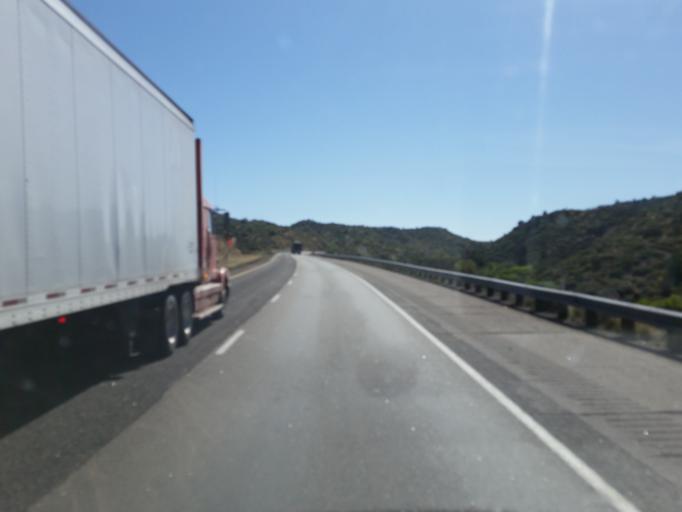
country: US
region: Arizona
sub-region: Mohave County
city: Peach Springs
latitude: 35.1757
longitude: -113.4936
